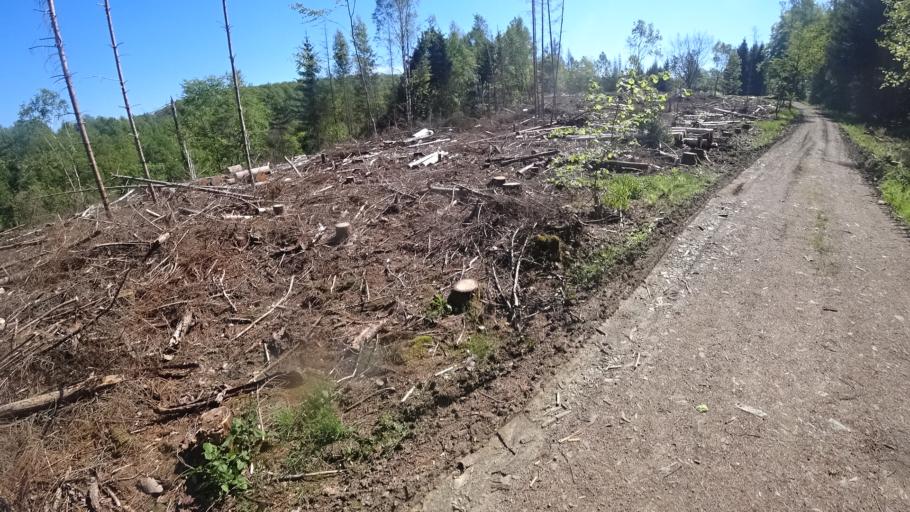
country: DE
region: Rheinland-Pfalz
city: Kausen
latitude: 50.7354
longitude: 7.8625
